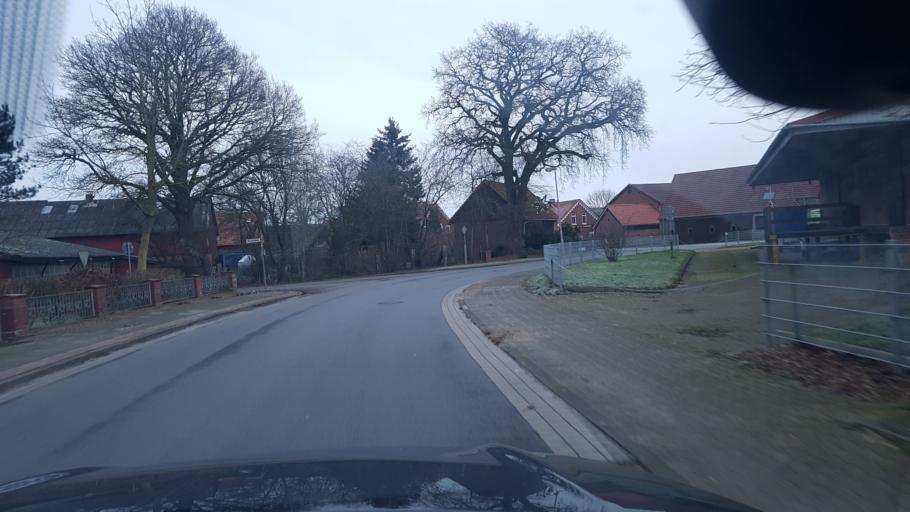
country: DE
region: Lower Saxony
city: Elmlohe
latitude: 53.6077
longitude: 8.6768
